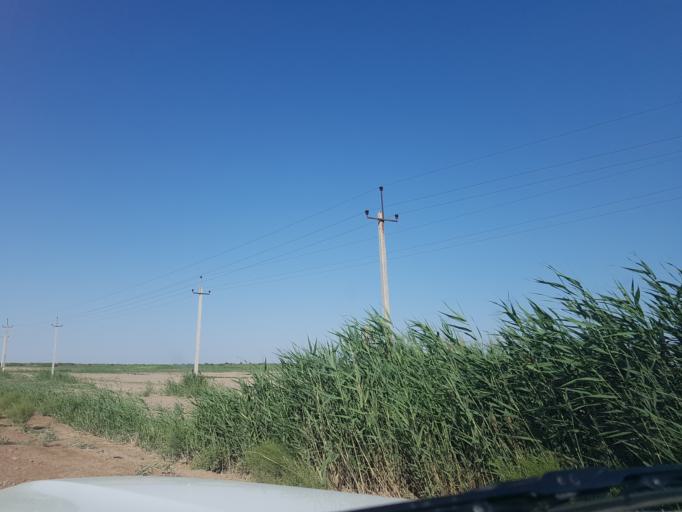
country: TM
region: Dasoguz
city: Koeneuergench
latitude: 42.1333
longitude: 58.9499
